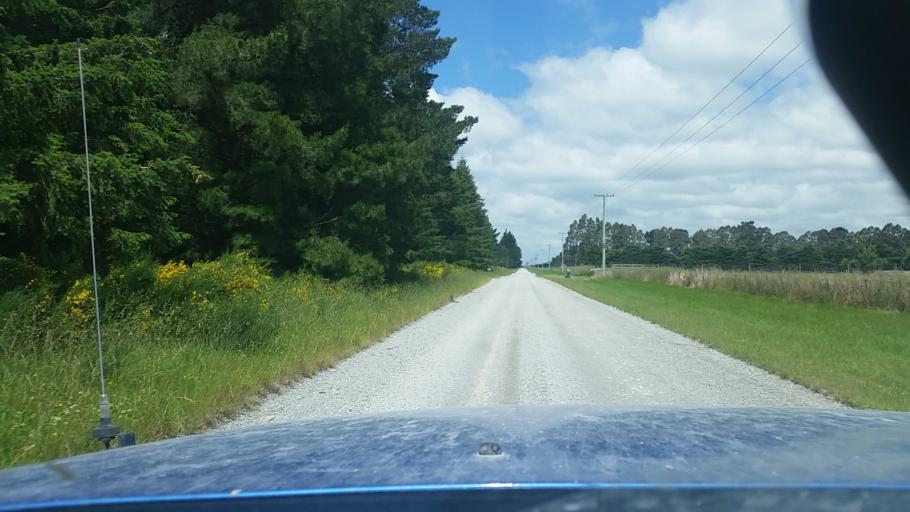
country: NZ
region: Canterbury
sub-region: Ashburton District
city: Methven
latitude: -43.8395
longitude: 171.3654
